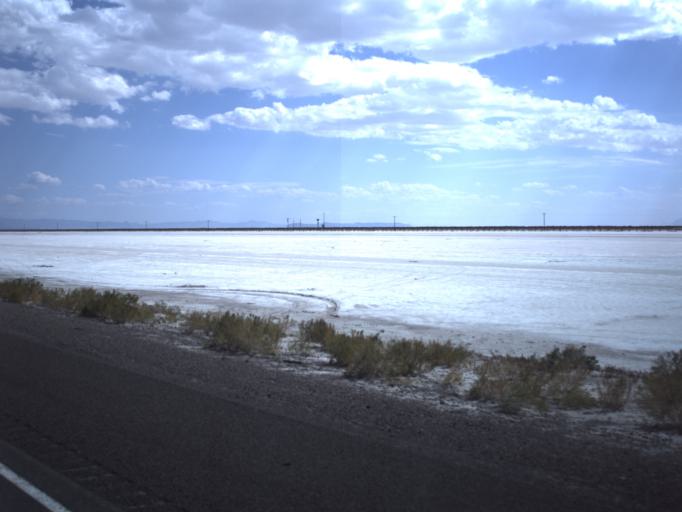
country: US
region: Utah
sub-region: Tooele County
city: Wendover
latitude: 40.7360
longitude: -113.7292
